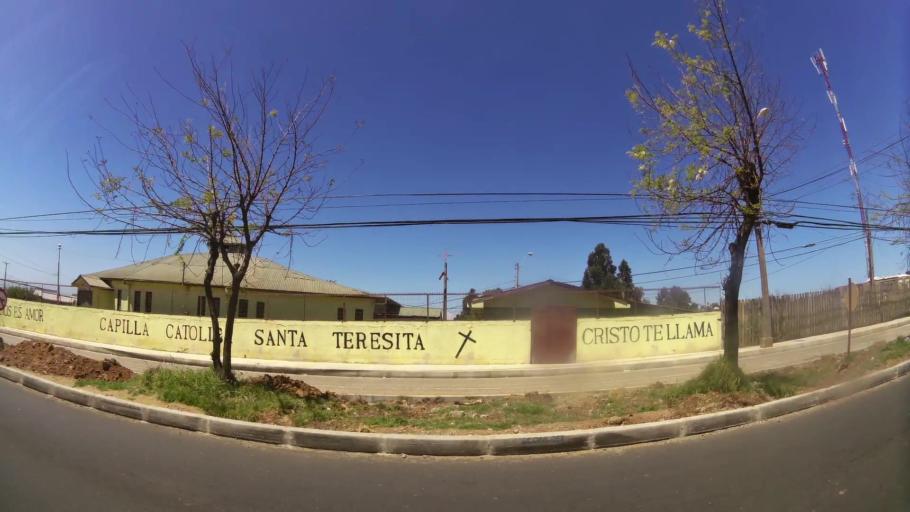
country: CL
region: Valparaiso
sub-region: Provincia de Valparaiso
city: Valparaiso
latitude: -33.0531
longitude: -71.6455
